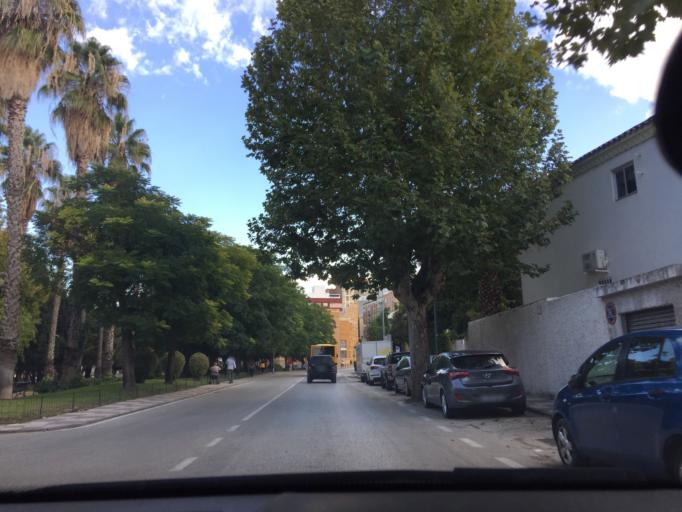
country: ES
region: Andalusia
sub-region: Provincia de Jaen
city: Jaen
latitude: 37.7794
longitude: -3.7939
